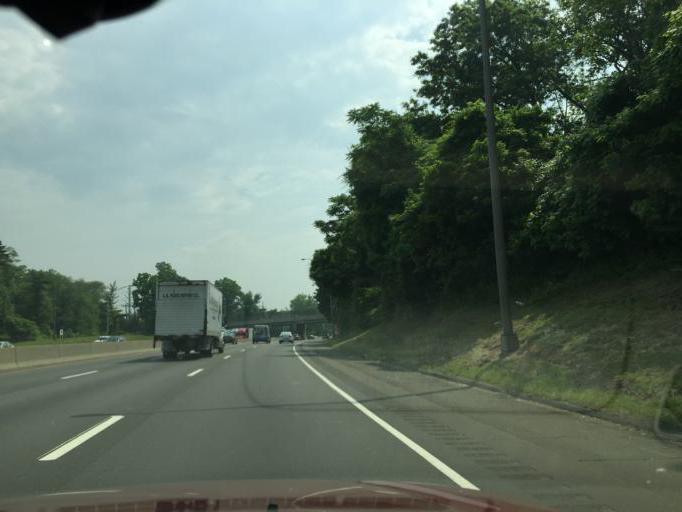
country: US
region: Connecticut
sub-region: Fairfield County
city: Darien
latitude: 41.0678
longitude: -73.5019
